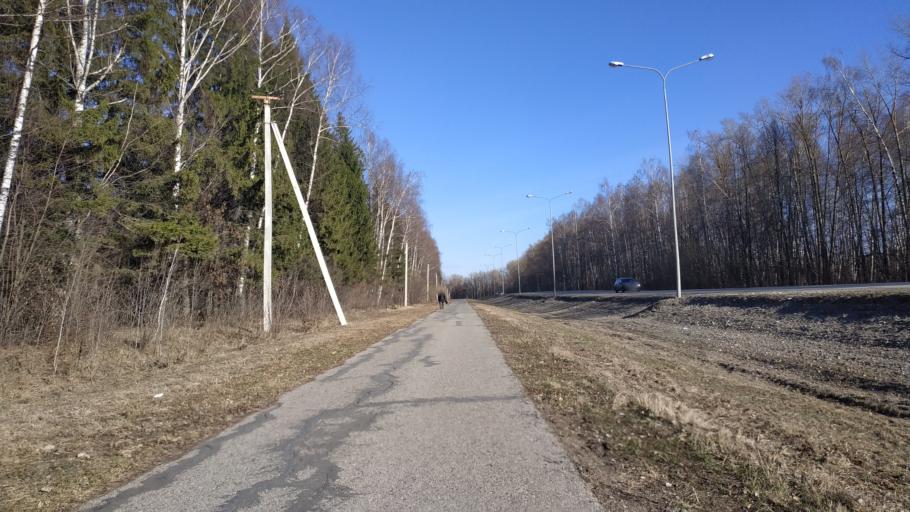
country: RU
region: Chuvashia
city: Novyye Lapsary
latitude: 56.1309
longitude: 47.1139
